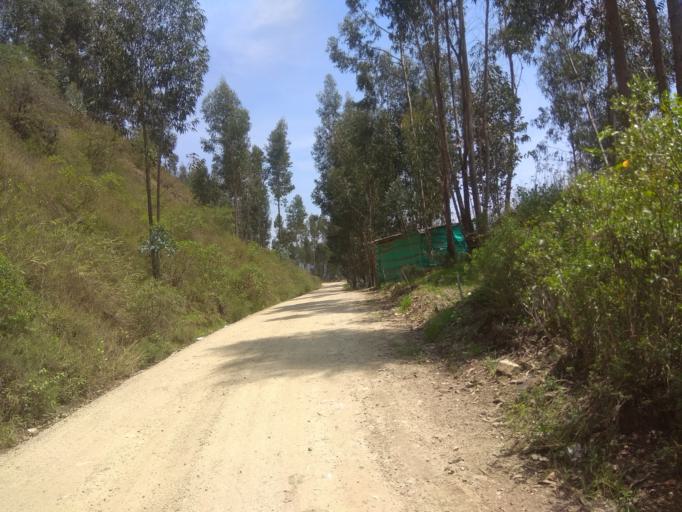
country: CO
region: Boyaca
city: Socha Viejo
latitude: 5.9782
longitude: -72.7300
